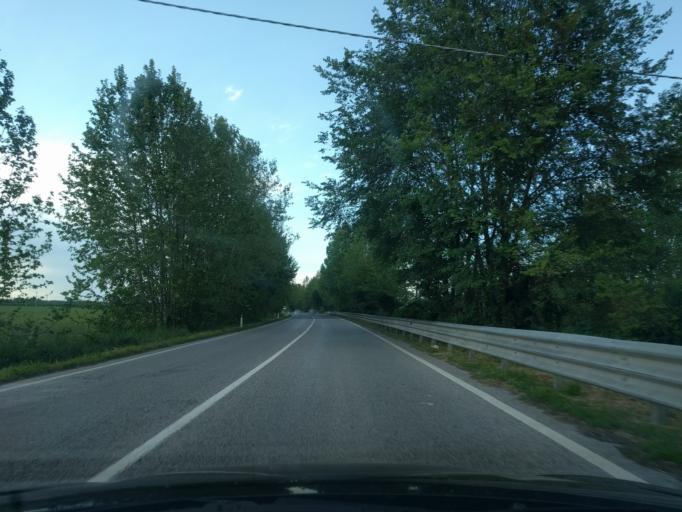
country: IT
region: Emilia-Romagna
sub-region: Provincia di Ferrara
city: Ro
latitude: 44.9411
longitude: 11.7334
